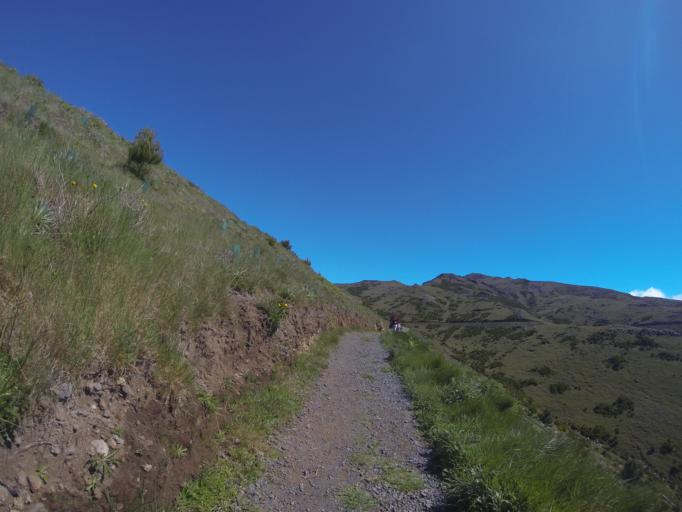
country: PT
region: Madeira
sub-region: Camara de Lobos
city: Curral das Freiras
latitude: 32.7148
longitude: -16.9546
